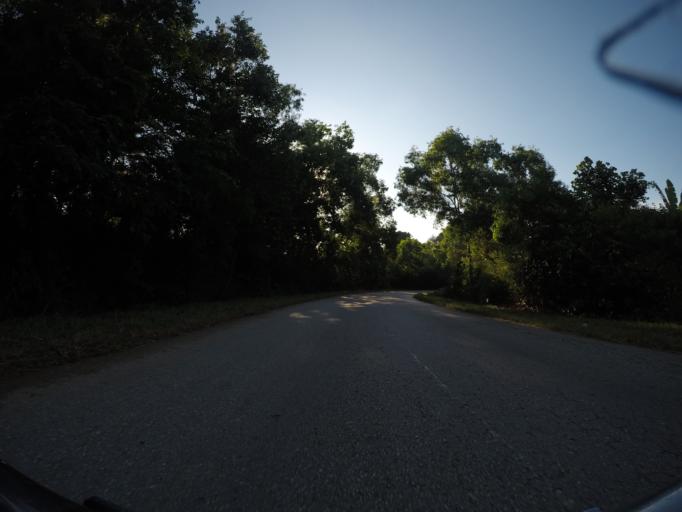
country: TZ
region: Pemba South
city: Uwelini
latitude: -5.3787
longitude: 39.6762
